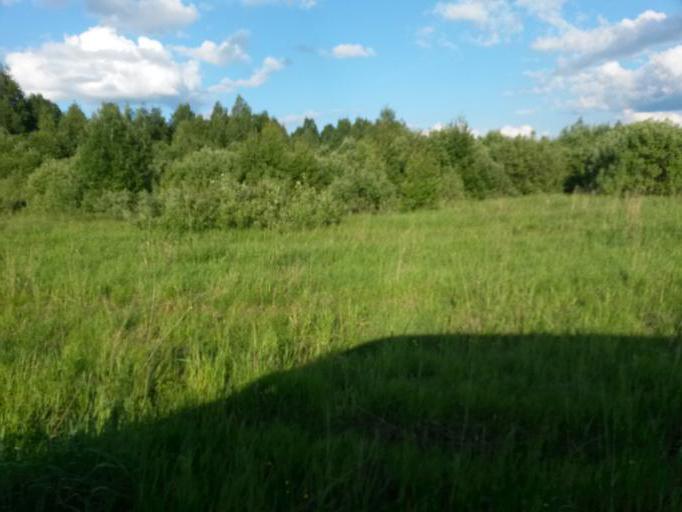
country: RU
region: Jaroslavl
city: Burmakino
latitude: 57.3661
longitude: 40.2010
